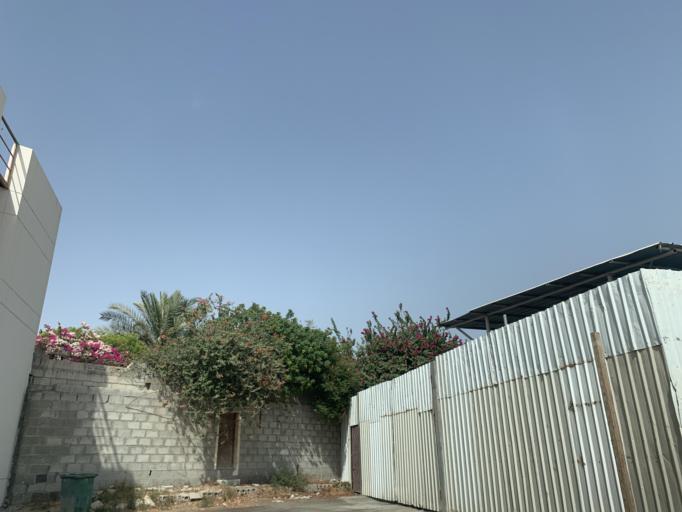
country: BH
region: Manama
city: Jidd Hafs
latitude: 26.2115
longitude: 50.5109
